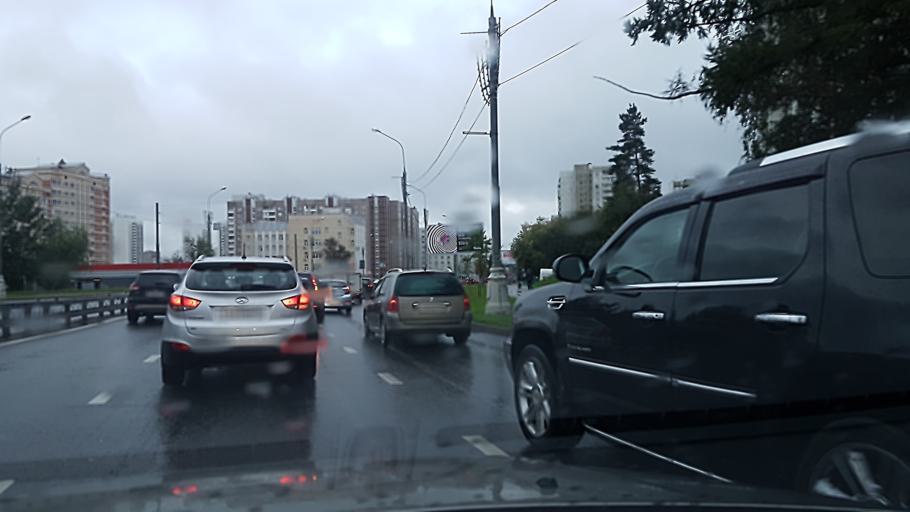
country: RU
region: Moscow
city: Zelenograd
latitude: 55.9774
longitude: 37.1665
